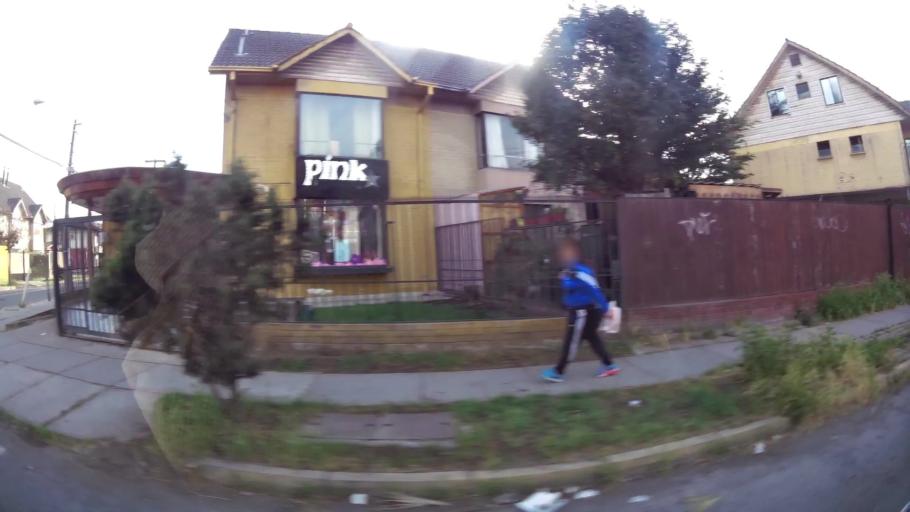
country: CL
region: Santiago Metropolitan
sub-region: Provincia de Maipo
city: San Bernardo
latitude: -33.5567
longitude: -70.7909
